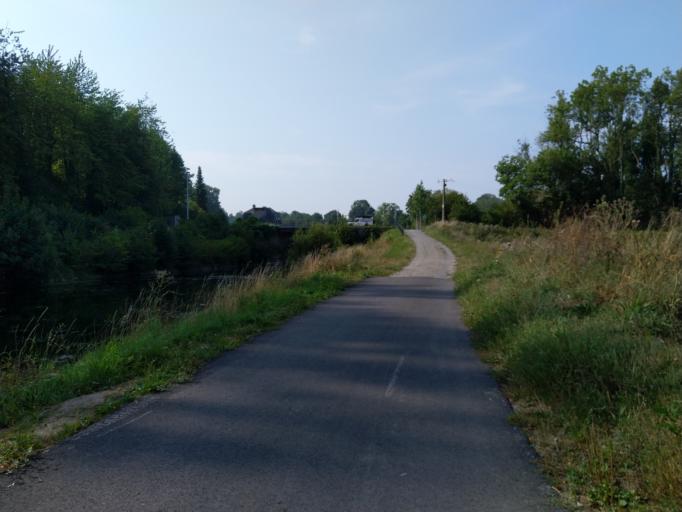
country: BE
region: Wallonia
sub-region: Province du Hainaut
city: Seneffe
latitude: 50.5785
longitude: 4.2529
